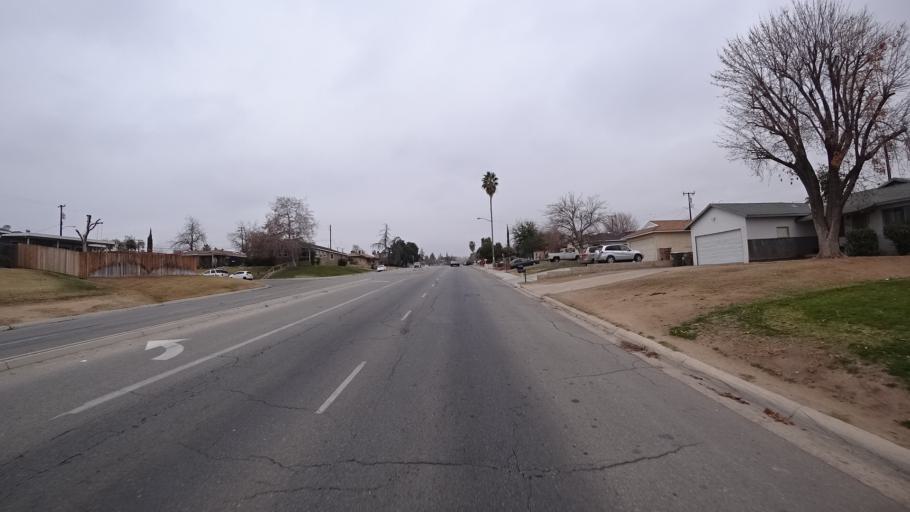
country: US
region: California
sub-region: Kern County
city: Bakersfield
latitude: 35.3779
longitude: -118.9319
